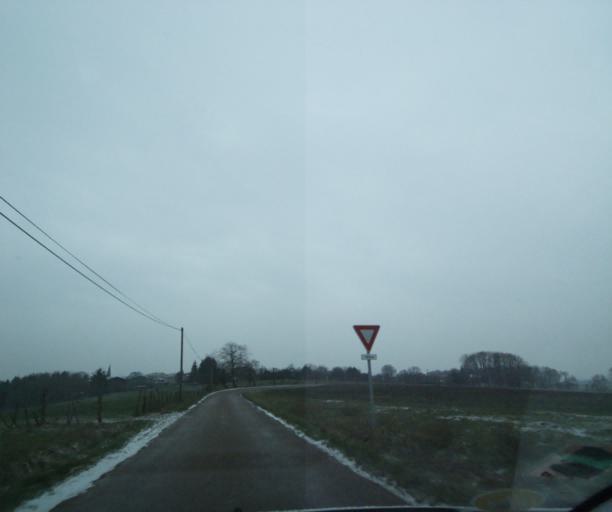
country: FR
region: Champagne-Ardenne
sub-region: Departement de la Haute-Marne
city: Wassy
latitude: 48.4639
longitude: 5.0343
